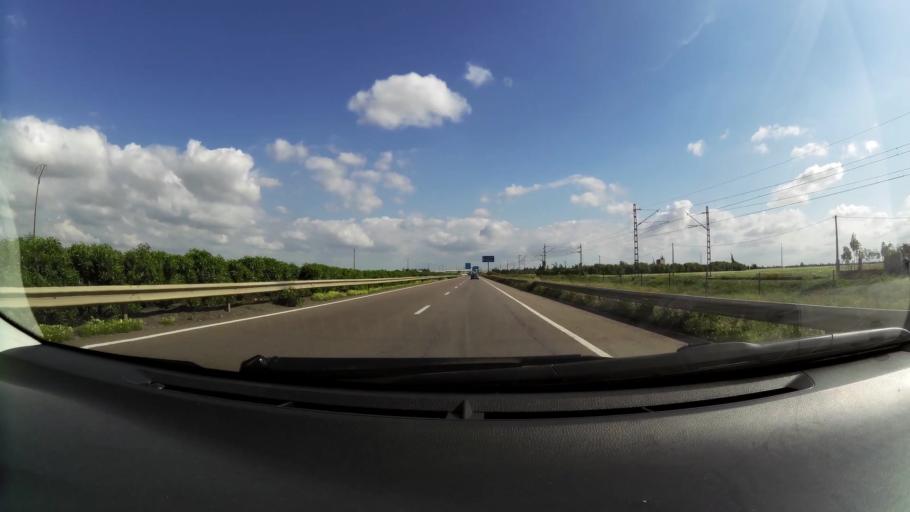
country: MA
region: Chaouia-Ouardigha
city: Nouaseur
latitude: 33.3312
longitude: -7.6086
